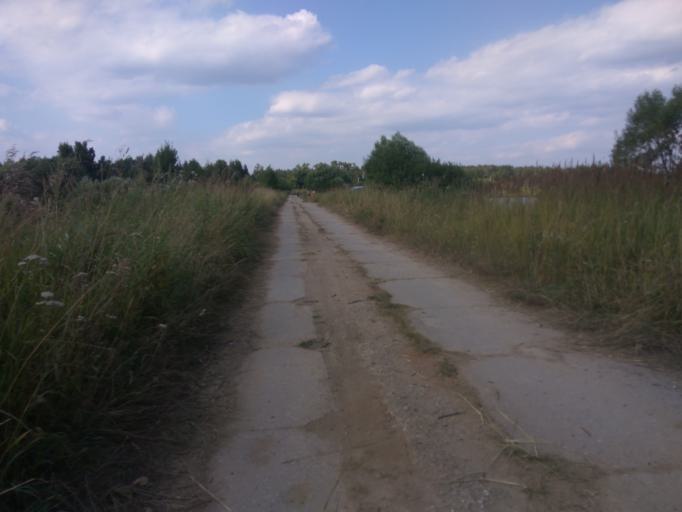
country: RU
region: Moskovskaya
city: Kubinka
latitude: 55.5843
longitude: 36.7410
